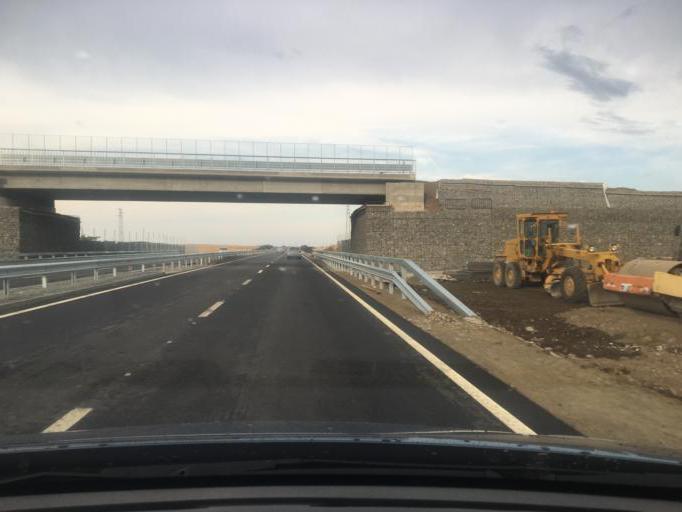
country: BG
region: Burgas
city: Aheloy
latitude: 42.6557
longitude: 27.6459
